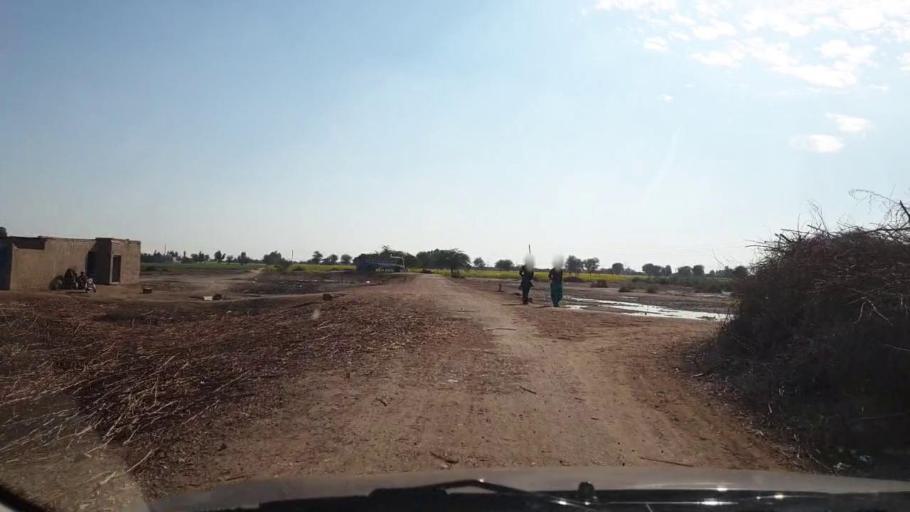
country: PK
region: Sindh
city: Sinjhoro
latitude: 26.0094
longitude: 68.8294
